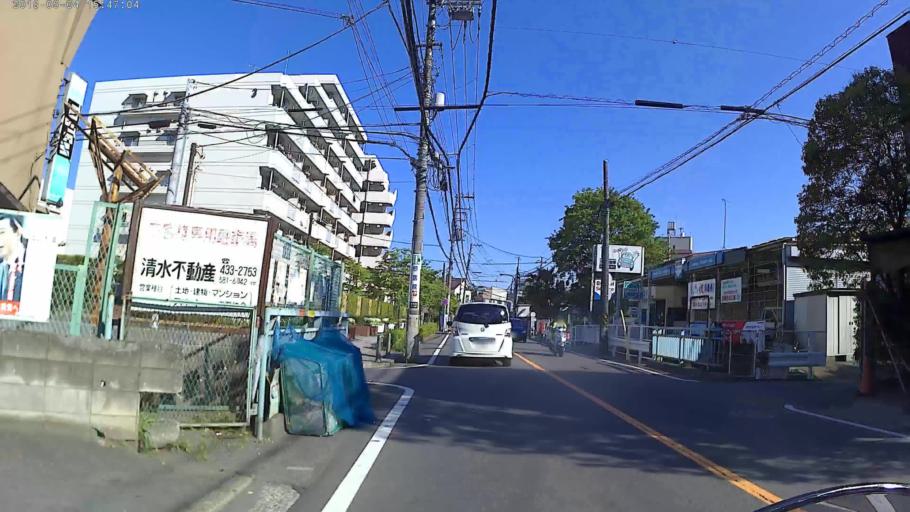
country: JP
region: Kanagawa
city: Yokohama
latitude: 35.4998
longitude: 139.6451
